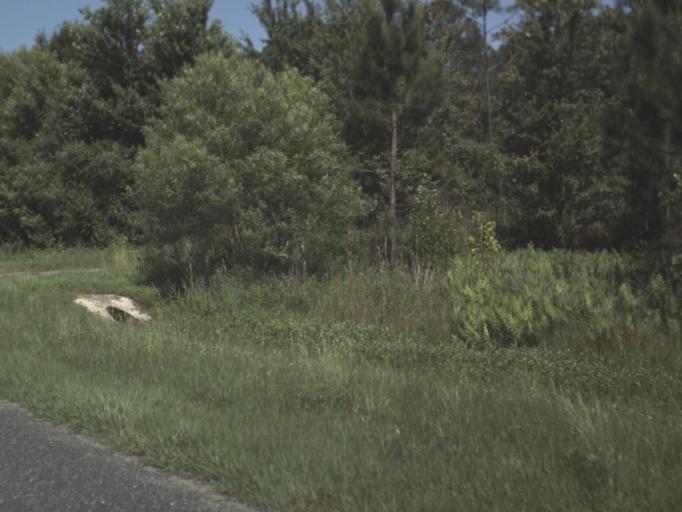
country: US
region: Florida
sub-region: Union County
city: Lake Butler
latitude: 30.2056
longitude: -82.4159
